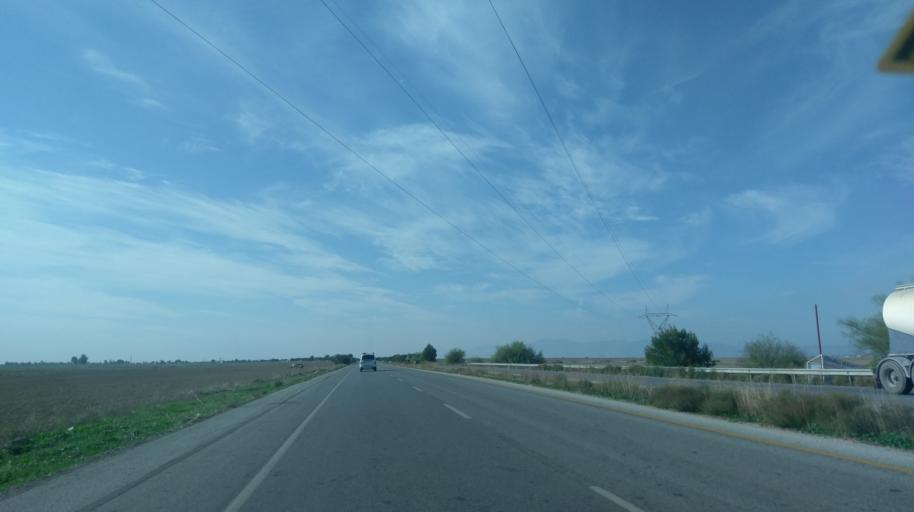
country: CY
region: Ammochostos
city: Acheritou
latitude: 35.1704
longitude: 33.8168
